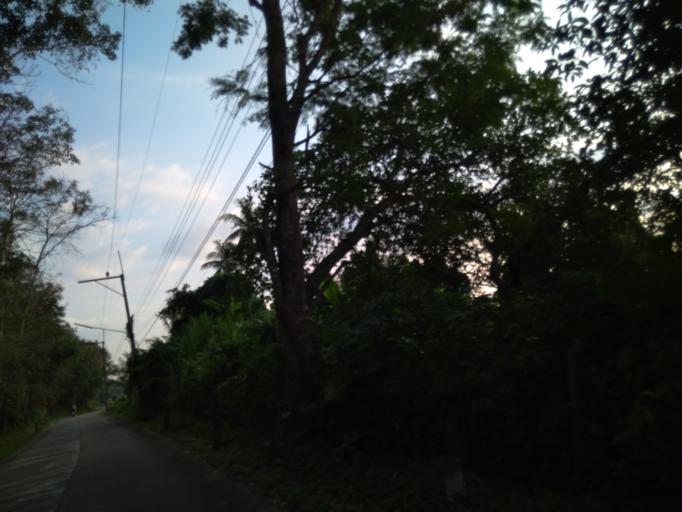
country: TH
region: Phangnga
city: Ko Yao
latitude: 8.1377
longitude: 98.5984
